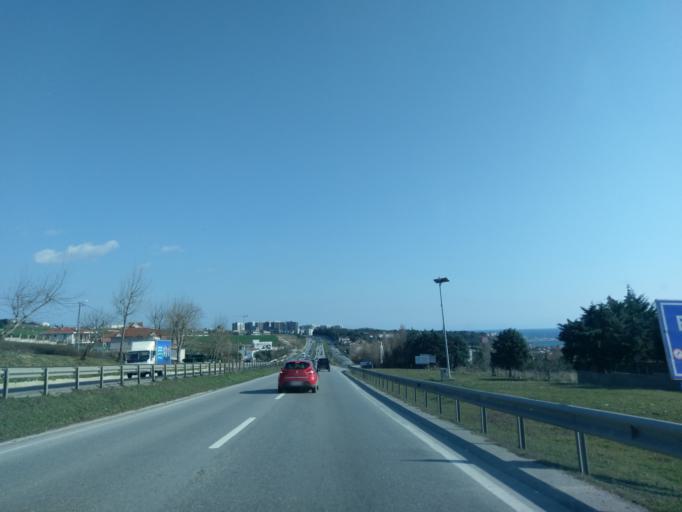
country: TR
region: Istanbul
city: Kumburgaz
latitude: 41.0123
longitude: 28.4963
